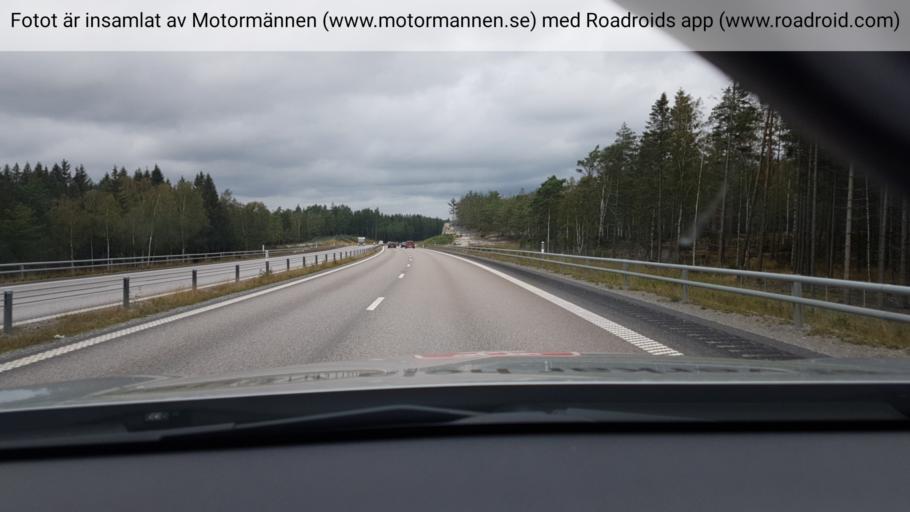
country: SE
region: Vaestra Goetaland
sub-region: Tanums Kommun
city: Tanumshede
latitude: 58.6718
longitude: 11.4116
